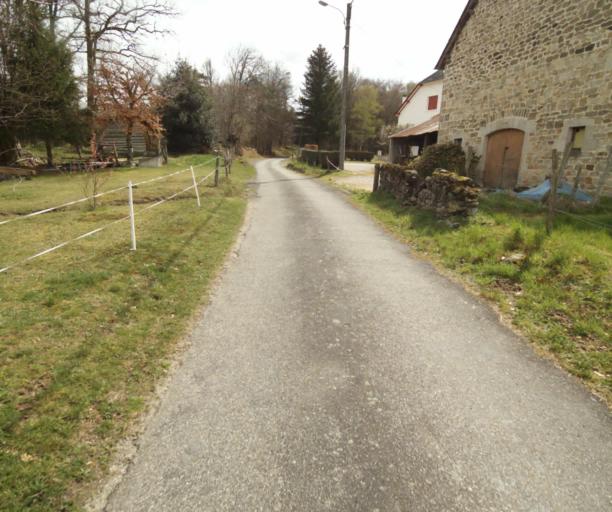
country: FR
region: Limousin
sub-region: Departement de la Correze
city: Laguenne
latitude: 45.2194
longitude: 1.8989
